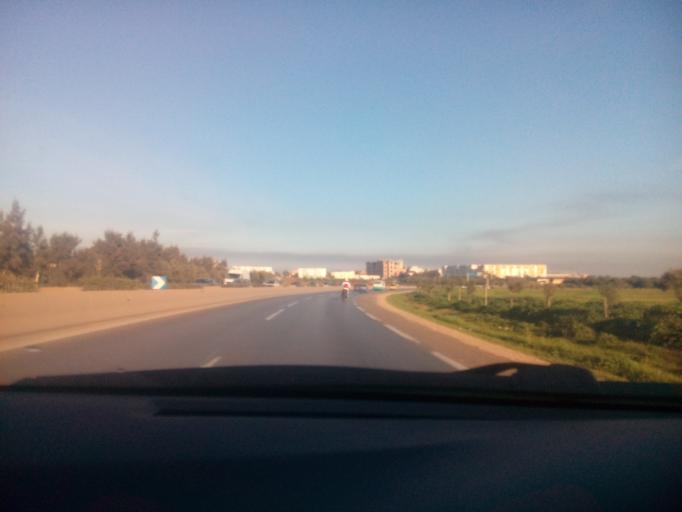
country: DZ
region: Oran
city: Bir el Djir
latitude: 35.7738
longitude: -0.4419
